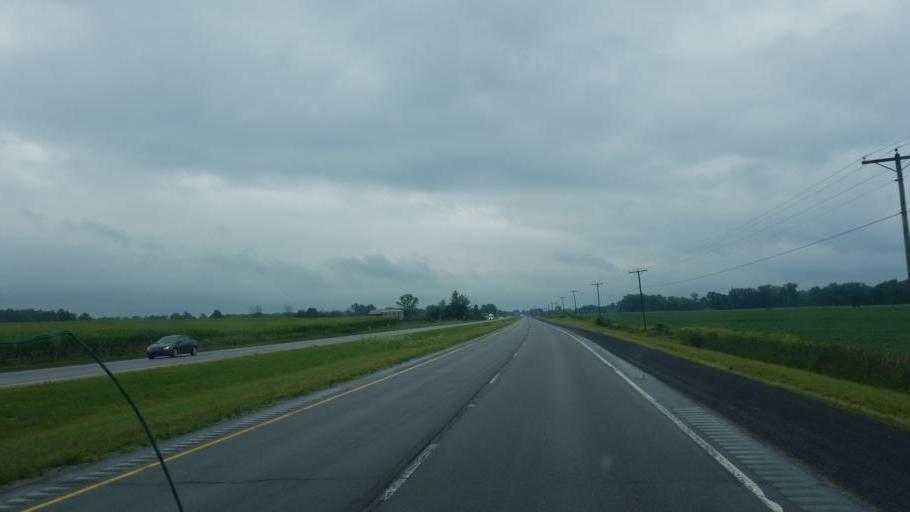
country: US
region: Indiana
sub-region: Wells County
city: Ossian
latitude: 40.9581
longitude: -85.0708
